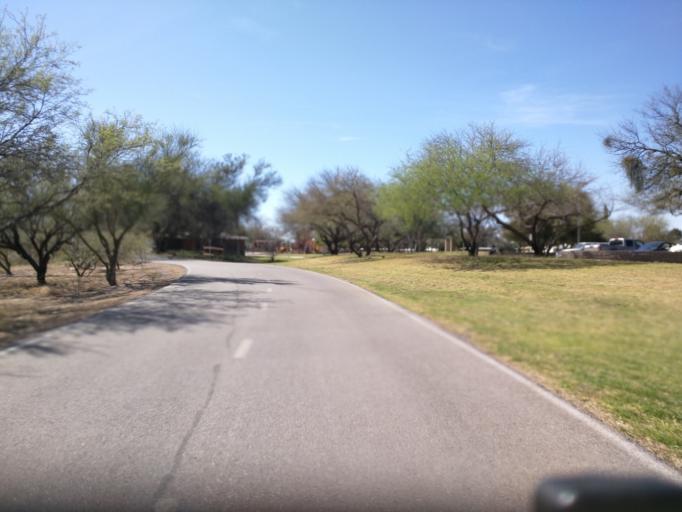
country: US
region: Arizona
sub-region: Pima County
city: Flowing Wells
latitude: 32.2951
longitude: -110.9838
